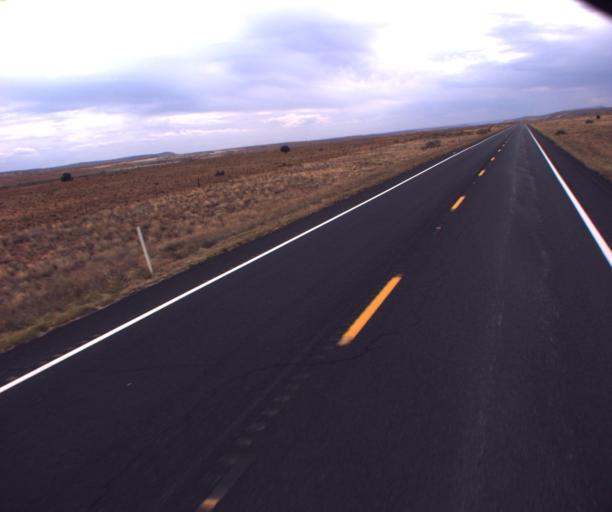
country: US
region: Arizona
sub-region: Coconino County
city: Kaibito
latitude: 36.3845
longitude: -110.8852
